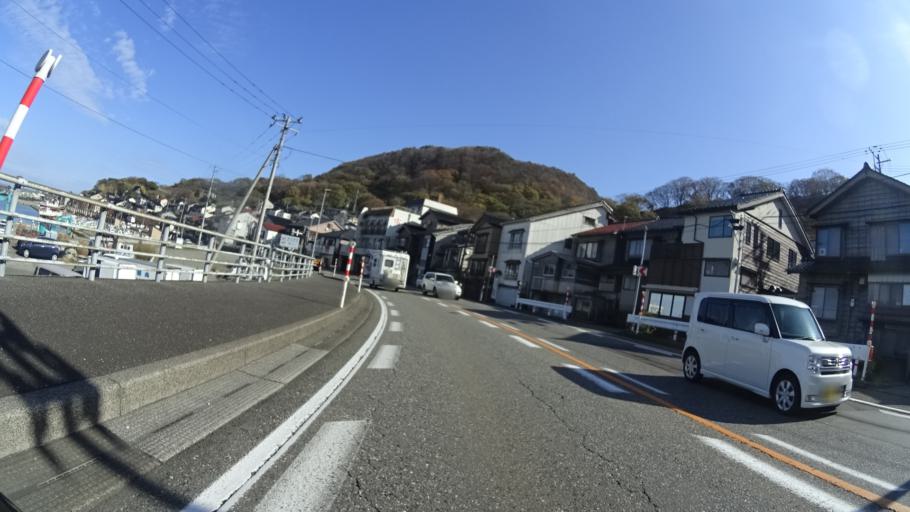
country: JP
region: Niigata
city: Itoigawa
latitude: 37.1084
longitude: 137.9988
